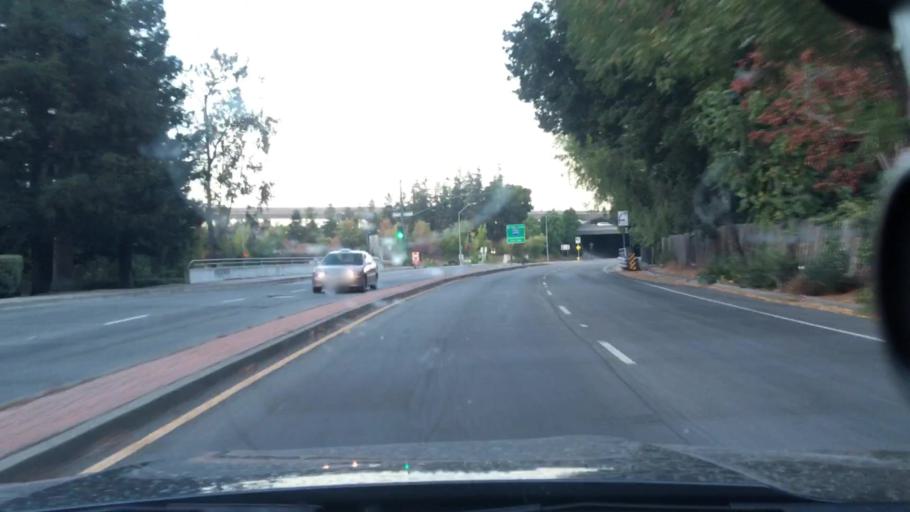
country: US
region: California
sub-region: Contra Costa County
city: Saranap
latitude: 37.8918
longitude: -122.0682
